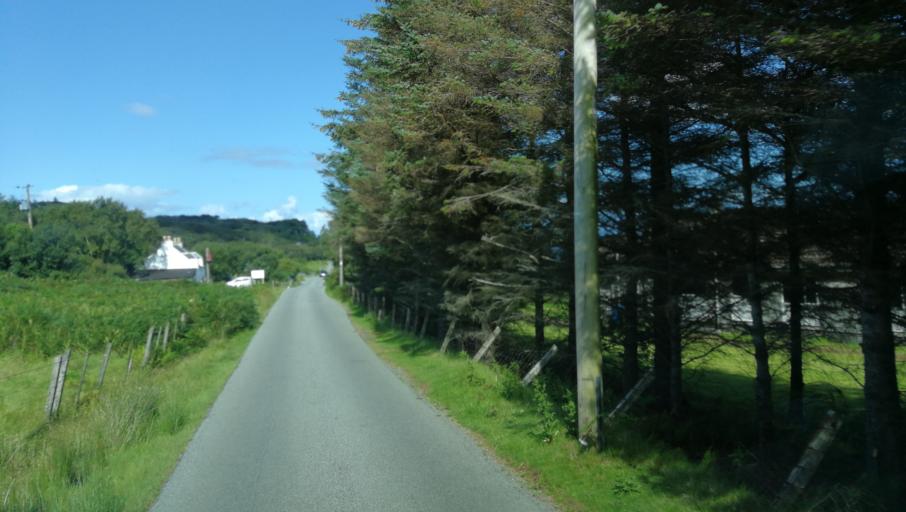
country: GB
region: Scotland
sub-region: Highland
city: Isle of Skye
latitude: 57.4419
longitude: -6.6397
